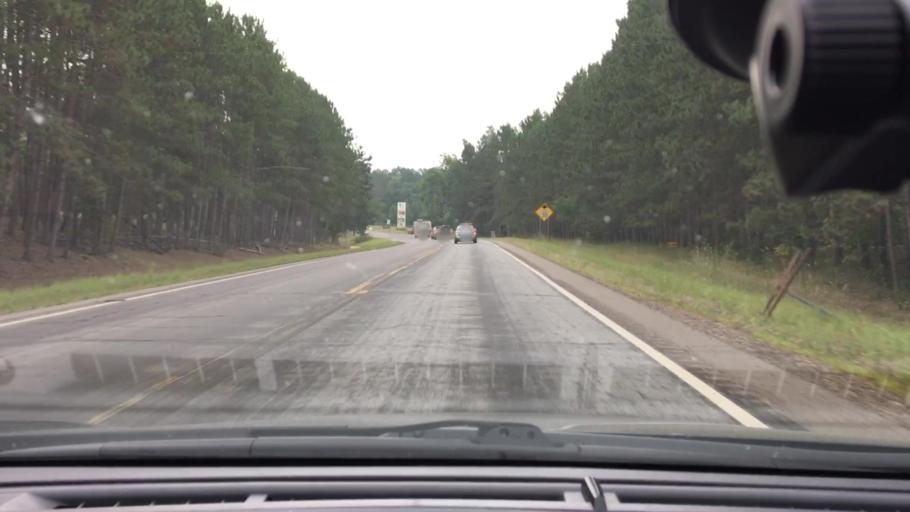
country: US
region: Minnesota
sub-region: Crow Wing County
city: Cross Lake
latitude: 46.7379
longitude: -93.9625
